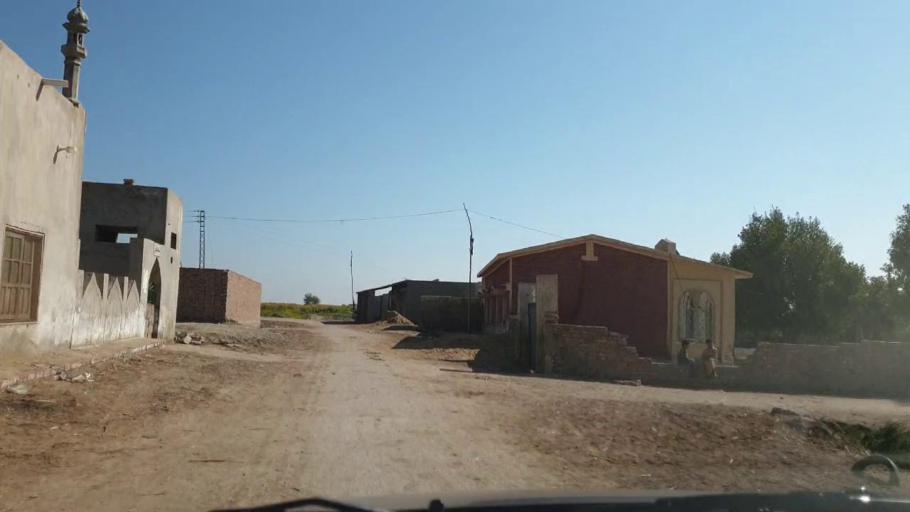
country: PK
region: Sindh
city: Sinjhoro
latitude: 26.1099
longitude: 68.8430
